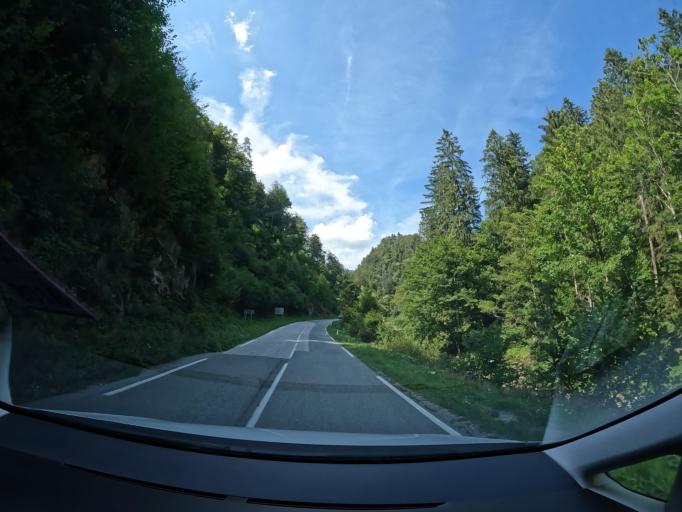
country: SI
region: Kranj
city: Golnik
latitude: 46.3854
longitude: 14.3728
